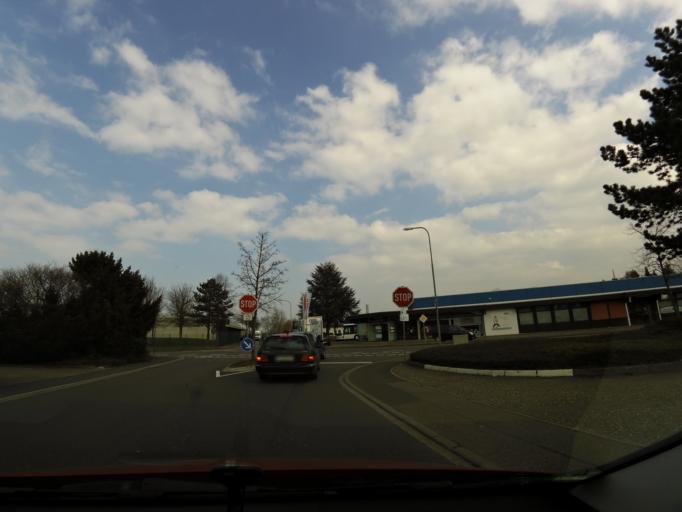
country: DE
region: Baden-Wuerttemberg
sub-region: Freiburg Region
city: Achern
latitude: 48.6369
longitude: 8.0628
